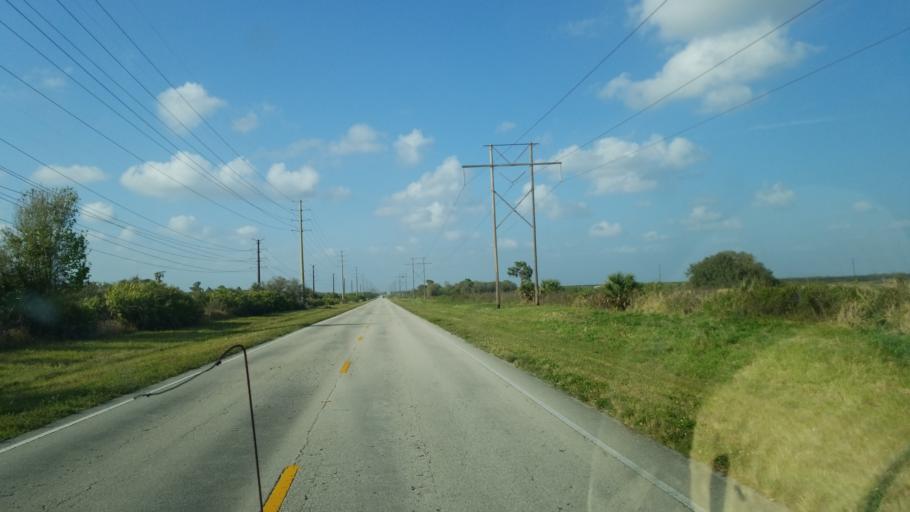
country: US
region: Florida
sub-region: Hardee County
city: Wauchula
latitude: 27.5536
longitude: -81.9321
